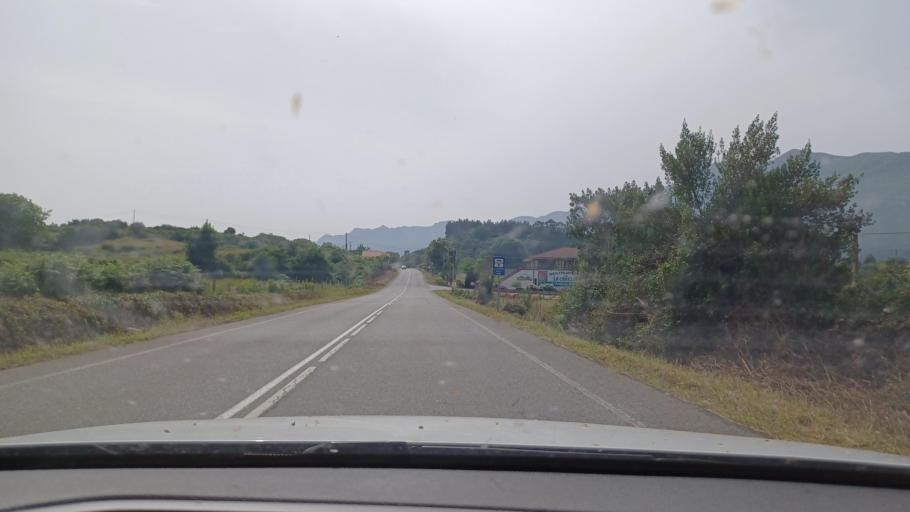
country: ES
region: Asturias
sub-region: Province of Asturias
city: Ribadesella
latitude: 43.4573
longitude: -5.0425
